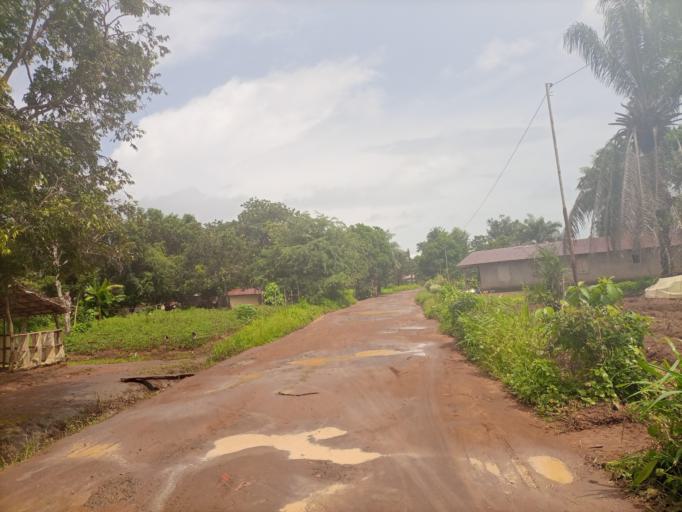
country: SL
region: Northern Province
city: Tintafor
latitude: 8.6359
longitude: -13.2164
